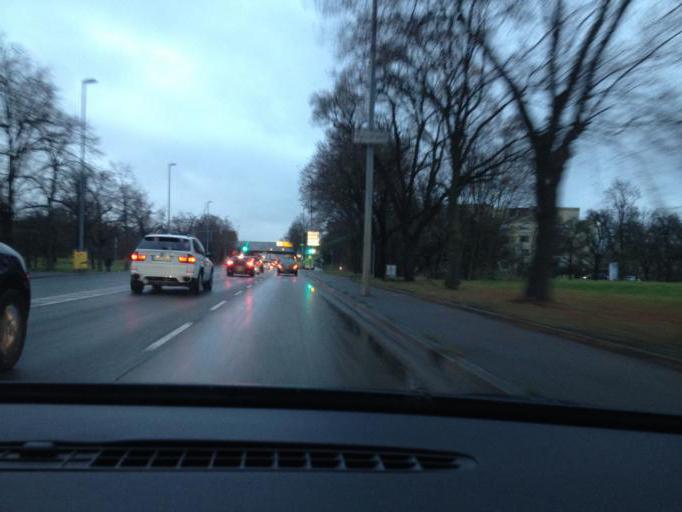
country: DE
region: Baden-Wuerttemberg
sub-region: Regierungsbezirk Stuttgart
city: Ludwigsburg
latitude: 48.9039
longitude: 9.1798
